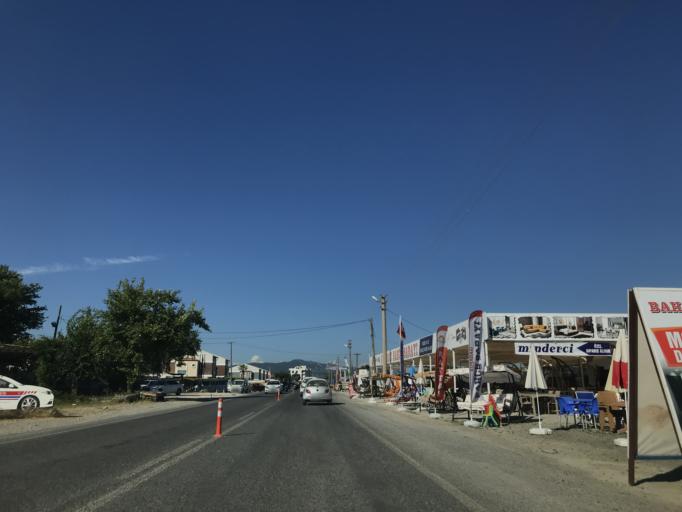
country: TR
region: Aydin
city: Davutlar
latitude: 37.7303
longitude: 27.2704
